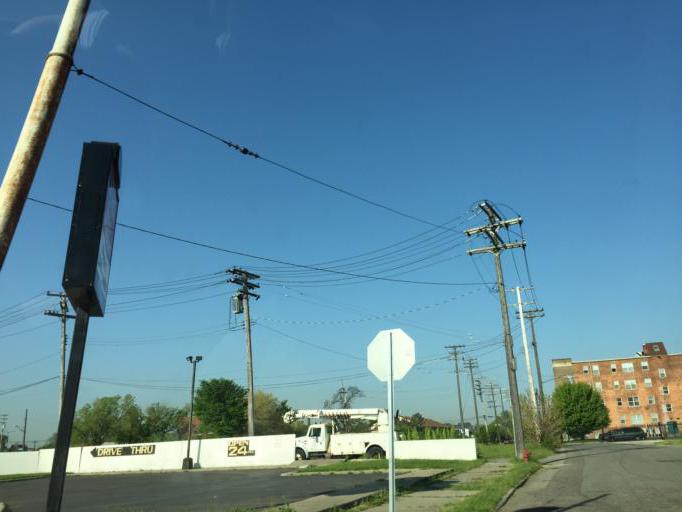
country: US
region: Michigan
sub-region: Wayne County
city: Detroit
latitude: 42.3428
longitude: -83.0749
